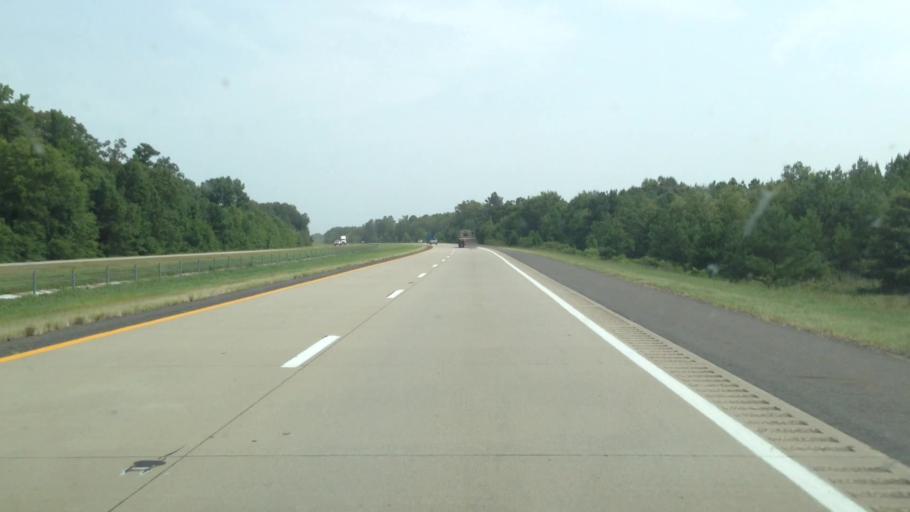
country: US
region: Texas
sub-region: Bowie County
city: Texarkana
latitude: 33.2091
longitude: -93.8747
